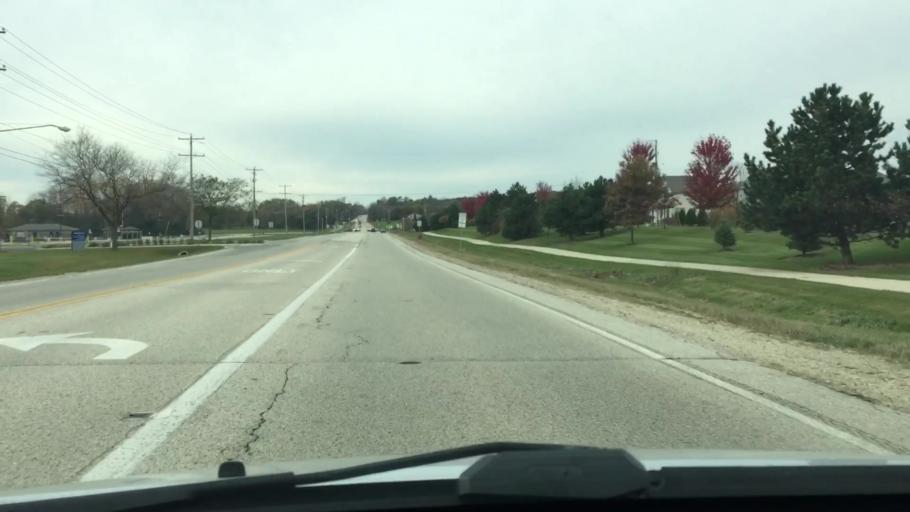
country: US
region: Wisconsin
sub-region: Waukesha County
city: Mukwonago
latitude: 42.8746
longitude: -88.3485
